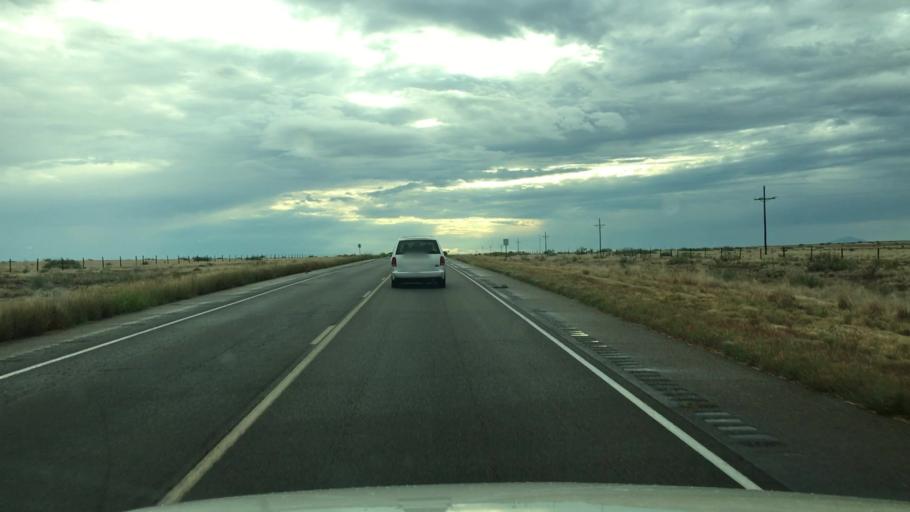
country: US
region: New Mexico
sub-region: Chaves County
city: Roswell
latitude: 33.4016
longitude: -104.3324
